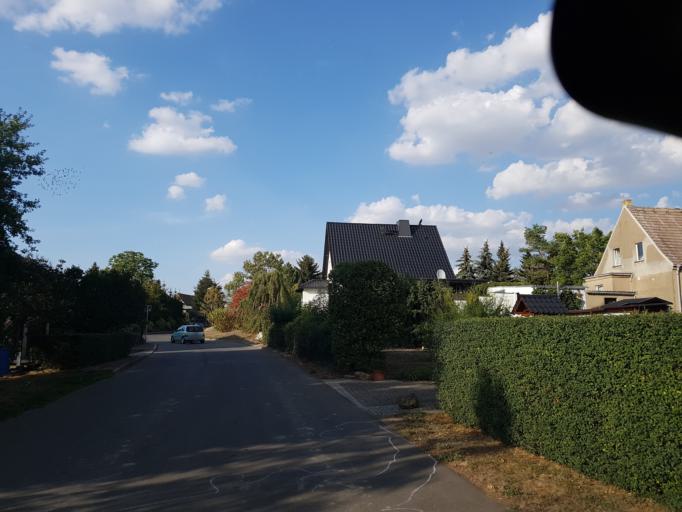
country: DE
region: Saxony
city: Oschatz
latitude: 51.2863
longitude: 13.1449
